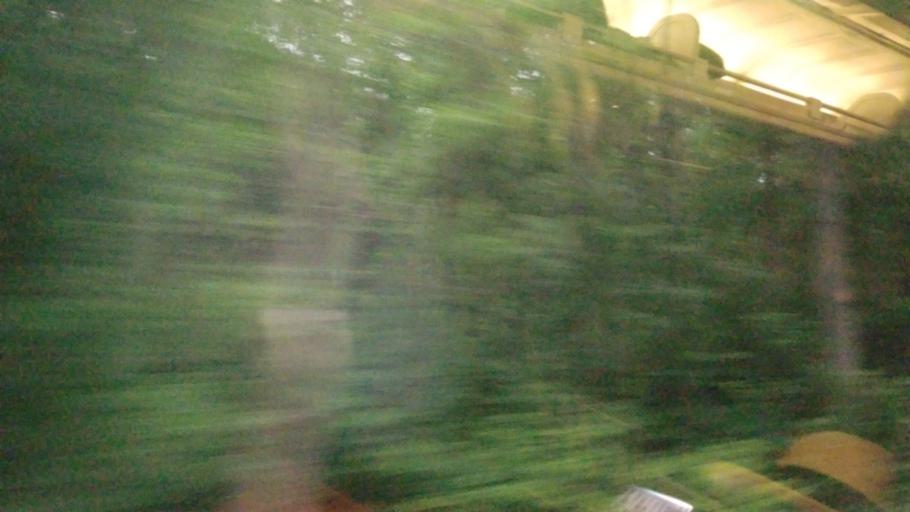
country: US
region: Virginia
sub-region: Orange County
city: Orange
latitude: 38.2818
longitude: -78.0937
